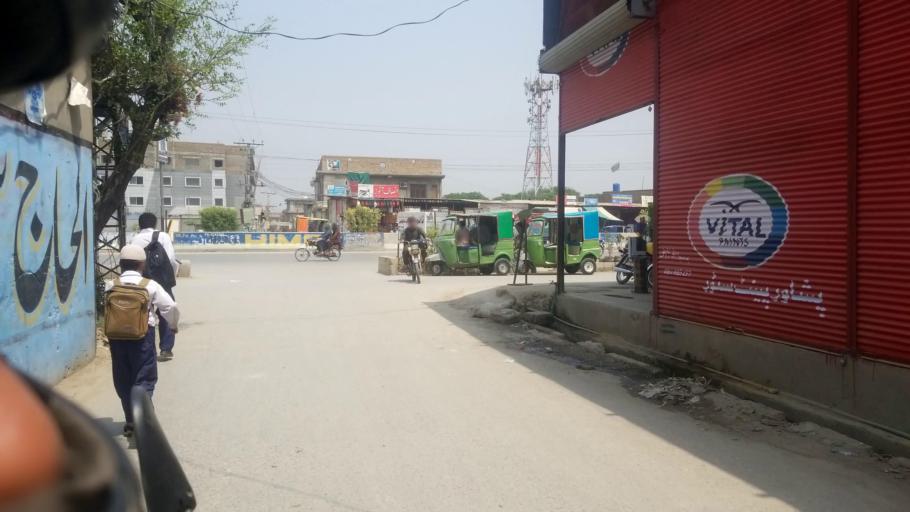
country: PK
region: Khyber Pakhtunkhwa
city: Peshawar
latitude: 34.0311
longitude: 71.5895
